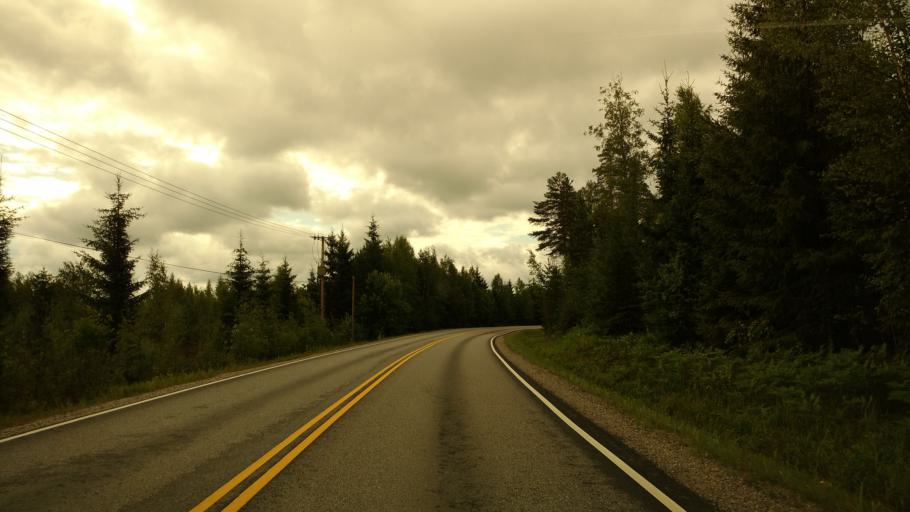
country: FI
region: Varsinais-Suomi
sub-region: Salo
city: Kuusjoki
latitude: 60.4504
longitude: 23.1752
